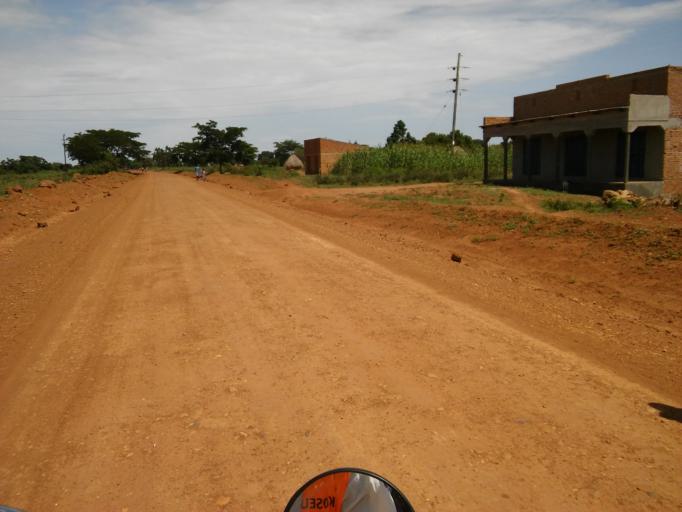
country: UG
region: Eastern Region
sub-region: Kumi District
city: Kumi
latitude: 1.4784
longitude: 33.8878
